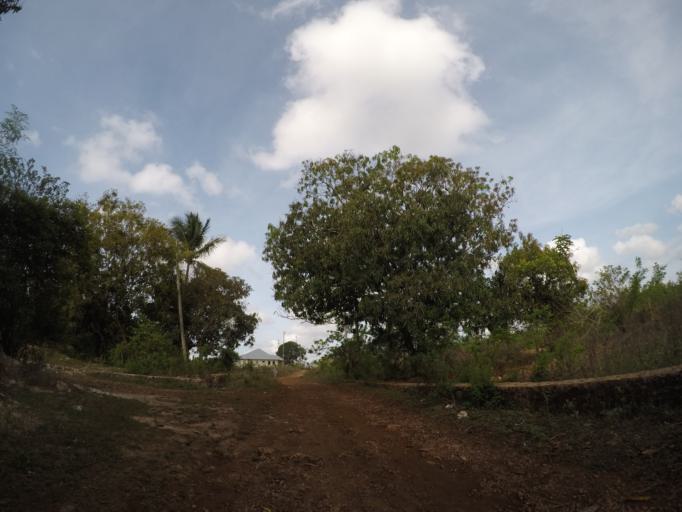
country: TZ
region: Zanzibar Central/South
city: Koani
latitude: -6.2281
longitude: 39.3130
